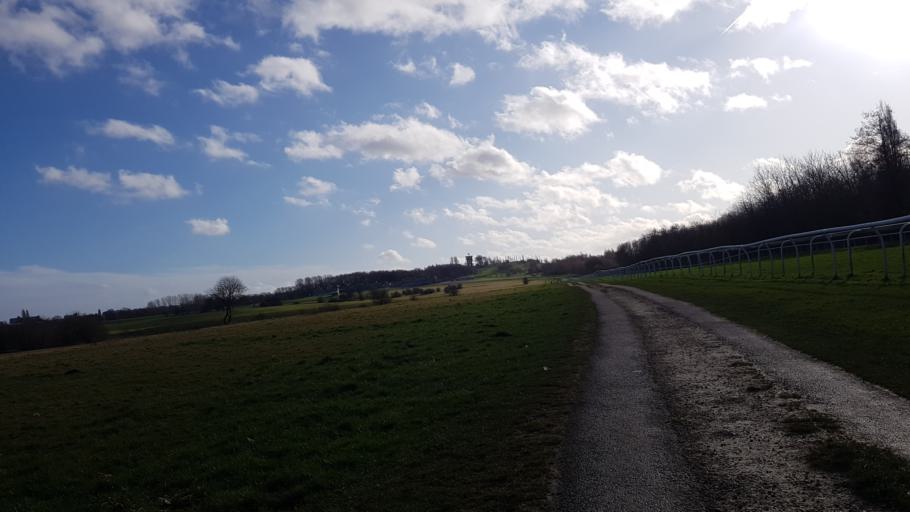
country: GB
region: England
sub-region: City and Borough of Wakefield
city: Pontefract
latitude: 53.7040
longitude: -1.3400
